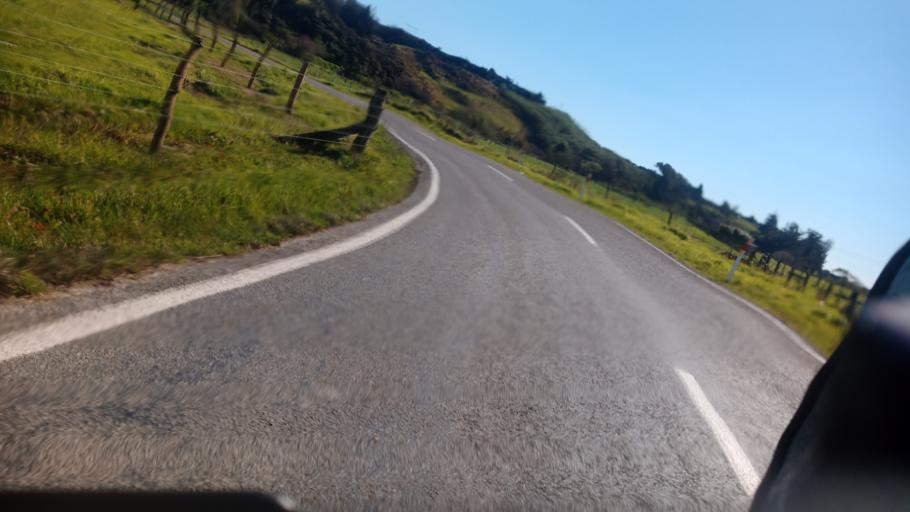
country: NZ
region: Bay of Plenty
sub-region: Opotiki District
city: Opotiki
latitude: -37.9956
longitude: 177.3924
